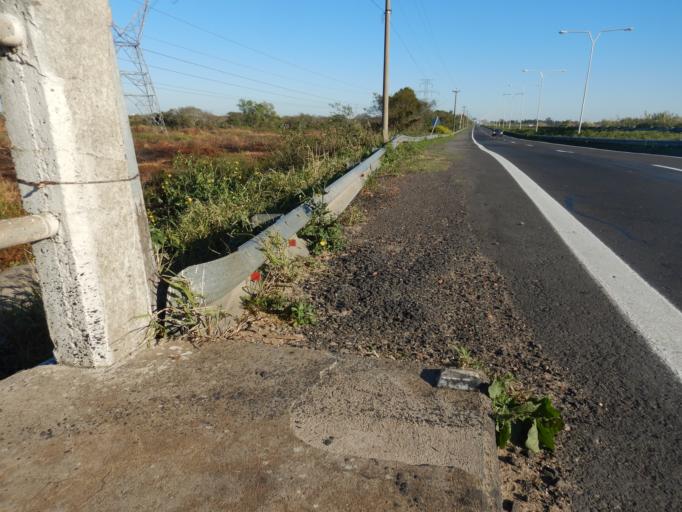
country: AR
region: Santa Fe
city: Santa Fe de la Vera Cruz
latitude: -31.6566
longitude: -60.6095
